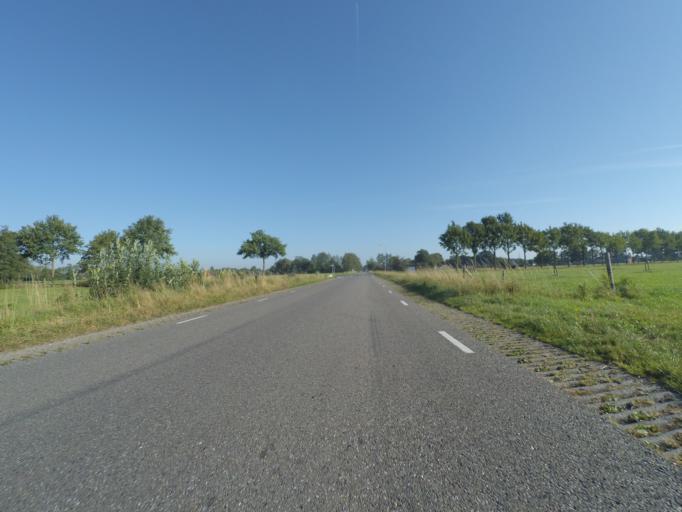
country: NL
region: Gelderland
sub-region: Gemeente Putten
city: Putten
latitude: 52.2328
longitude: 5.5772
